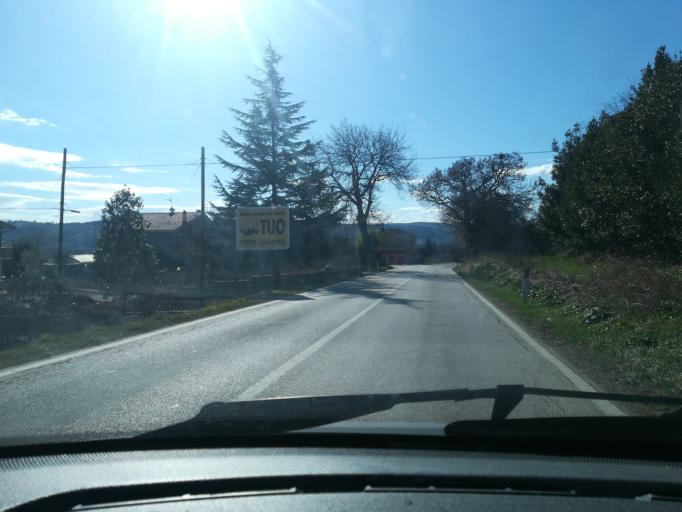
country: IT
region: The Marches
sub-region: Provincia di Macerata
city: Montecassiano
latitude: 43.3568
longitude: 13.4405
